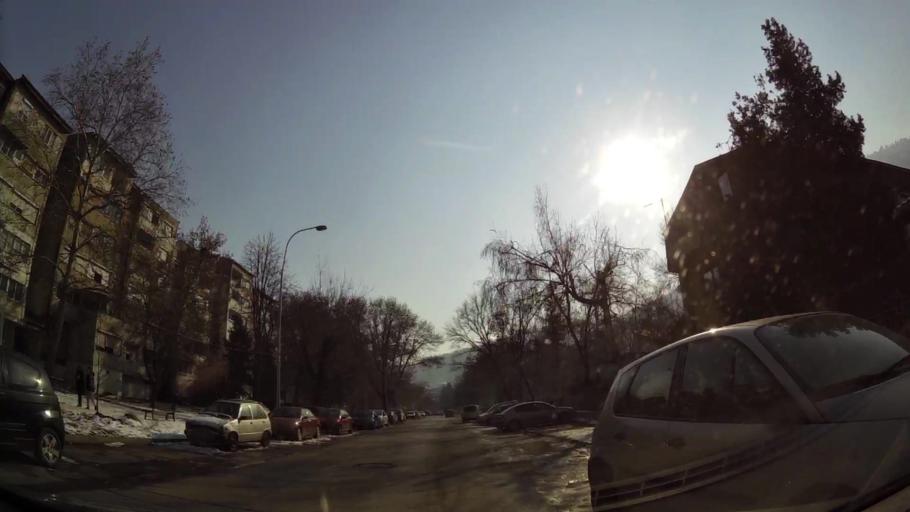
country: MK
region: Kisela Voda
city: Usje
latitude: 41.9741
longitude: 21.4411
